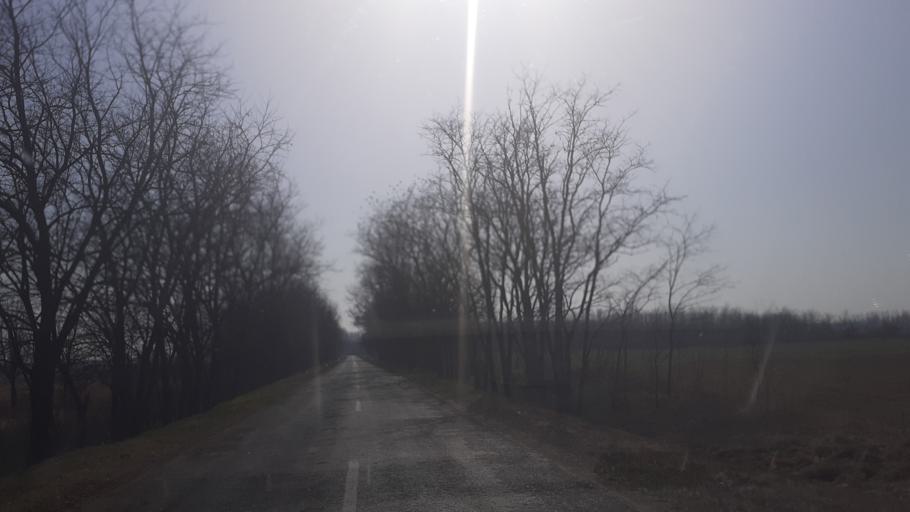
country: HU
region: Pest
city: Orkeny
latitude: 47.0987
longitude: 19.3600
